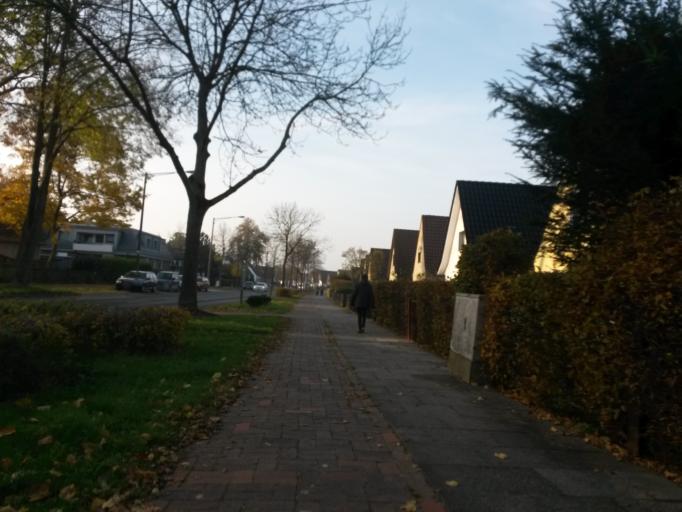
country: DE
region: Bremen
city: Bremen
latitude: 53.0281
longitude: 8.8184
